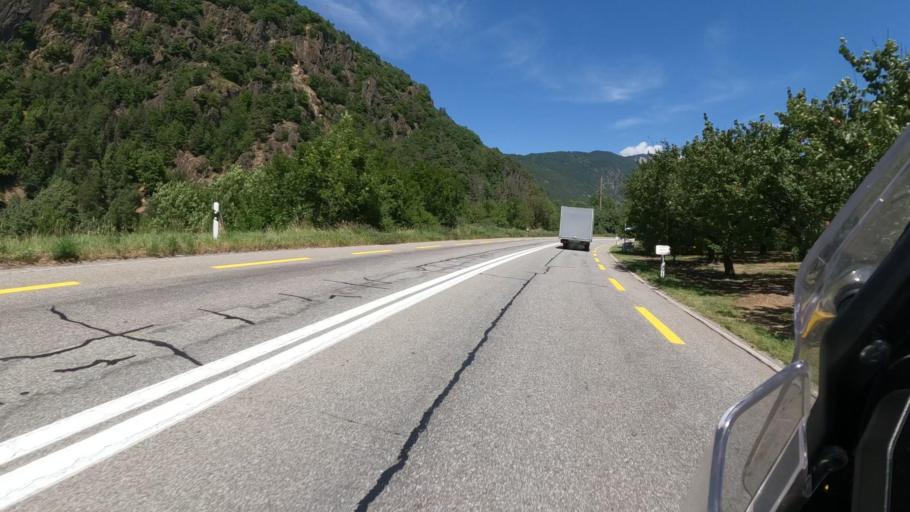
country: CH
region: Valais
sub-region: Martigny District
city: Martigny-Combe
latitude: 46.0744
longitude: 7.0670
